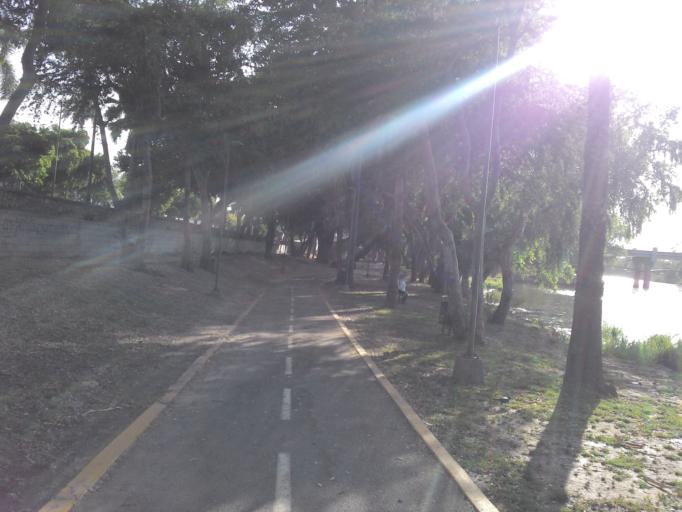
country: MX
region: Sinaloa
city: Culiacan
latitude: 24.8118
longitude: -107.4003
